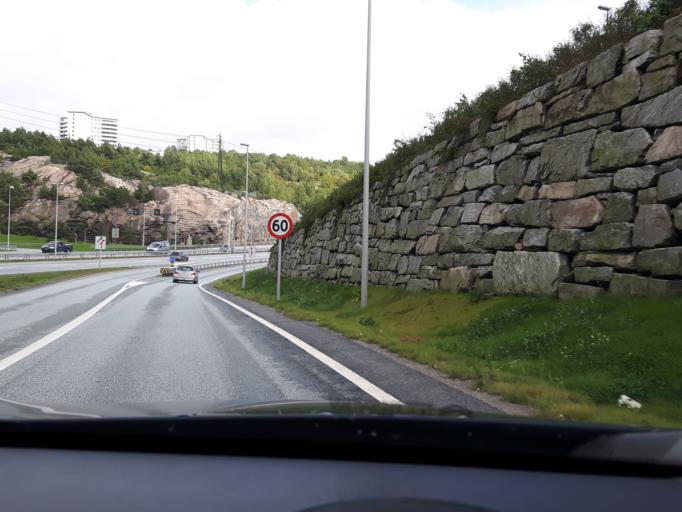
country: NO
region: Vest-Agder
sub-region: Kristiansand
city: Kristiansand
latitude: 58.1396
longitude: 7.9657
